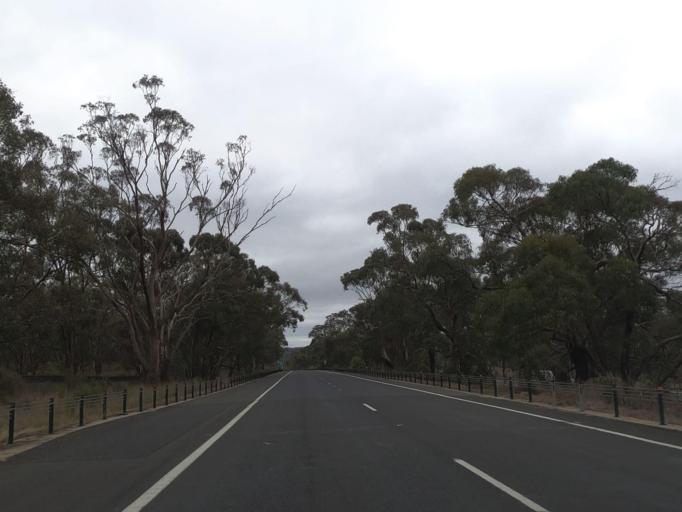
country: AU
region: Victoria
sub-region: Greater Bendigo
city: Kangaroo Flat
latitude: -36.9024
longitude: 144.2183
